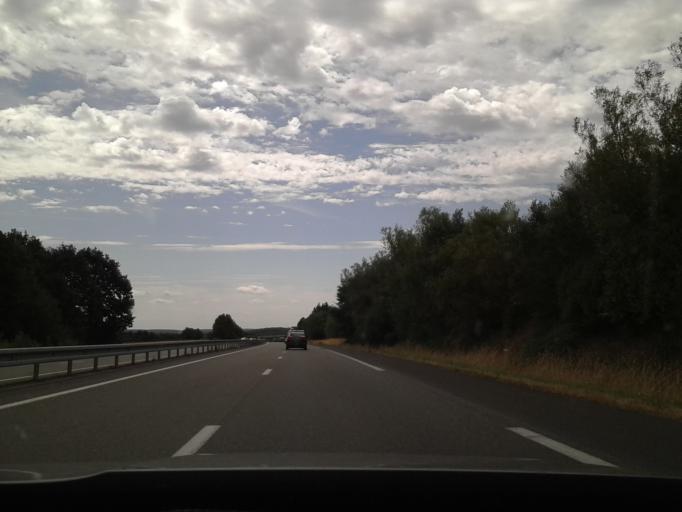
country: FR
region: Pays de la Loire
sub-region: Departement de la Sarthe
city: La Bazoge
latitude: 48.1155
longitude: 0.1513
